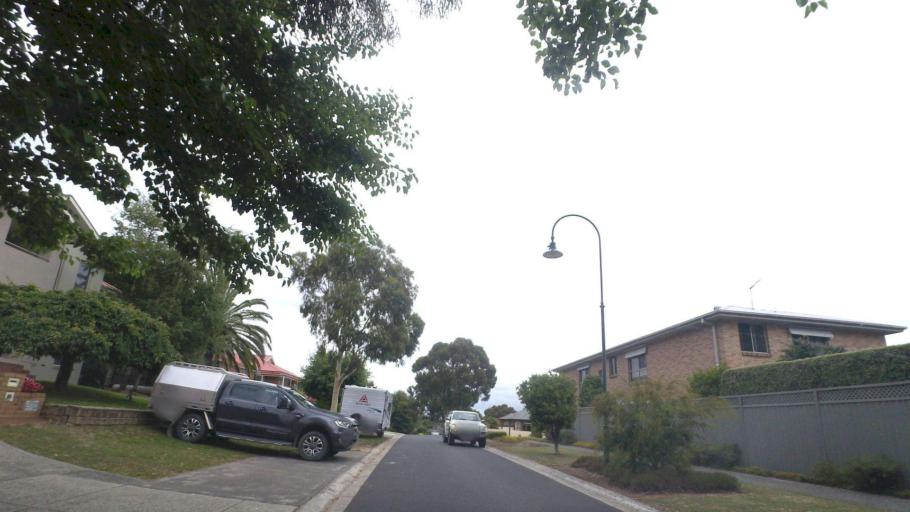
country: AU
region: Victoria
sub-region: Knox
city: The Basin
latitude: -37.8506
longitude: 145.3124
